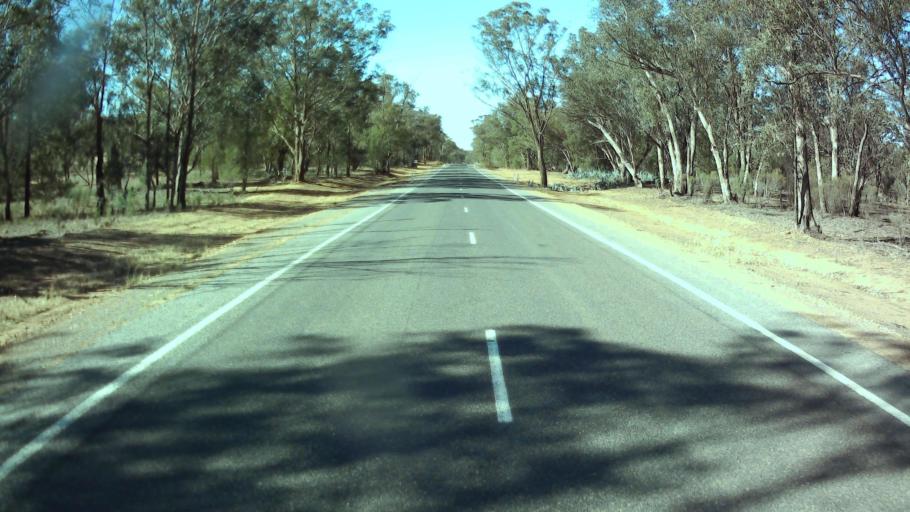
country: AU
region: New South Wales
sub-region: Weddin
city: Grenfell
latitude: -33.7528
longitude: 148.0838
